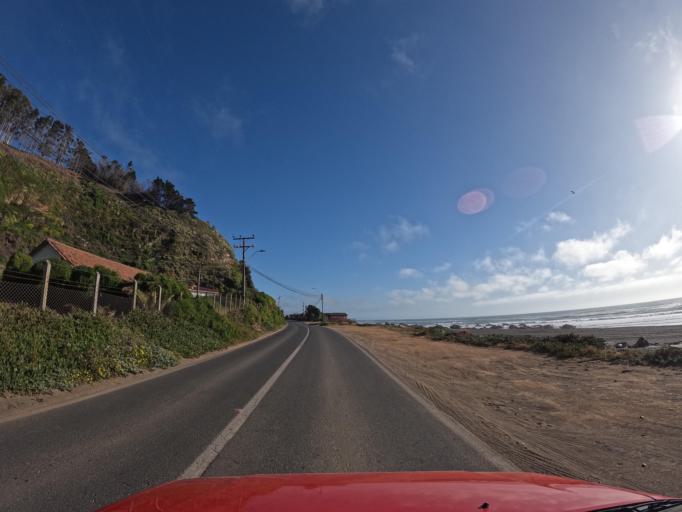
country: CL
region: Maule
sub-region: Provincia de Talca
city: Constitucion
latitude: -34.9140
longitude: -72.1819
